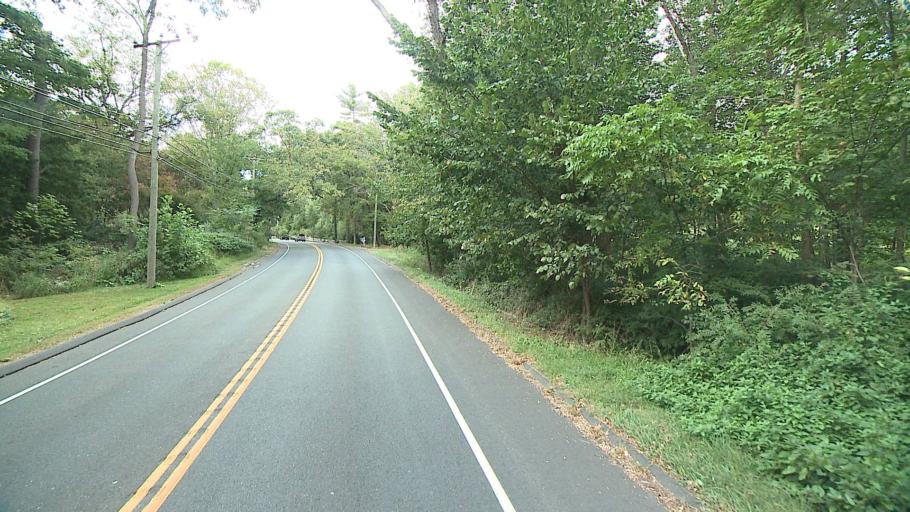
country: US
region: Connecticut
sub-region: Fairfield County
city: Westport
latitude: 41.1727
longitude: -73.3881
